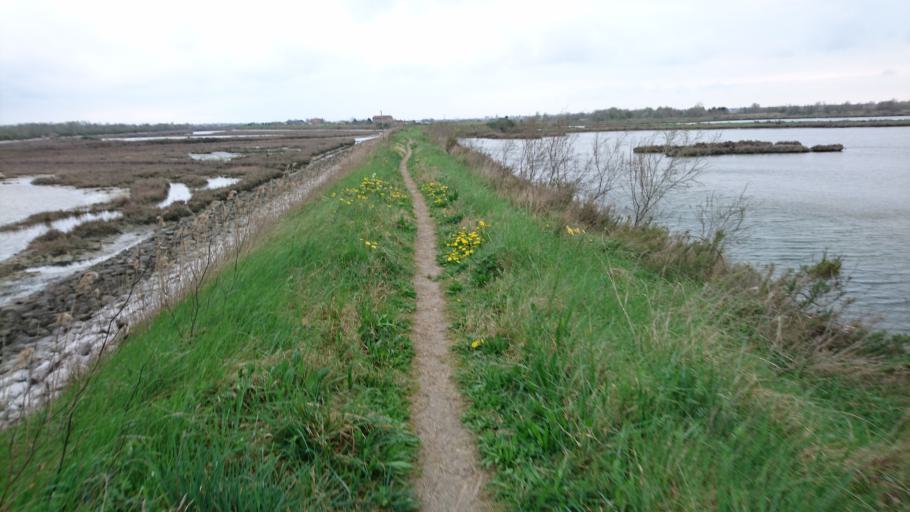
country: IT
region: Veneto
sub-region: Provincia di Venezia
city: Cavallino
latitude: 45.4966
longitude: 12.5008
